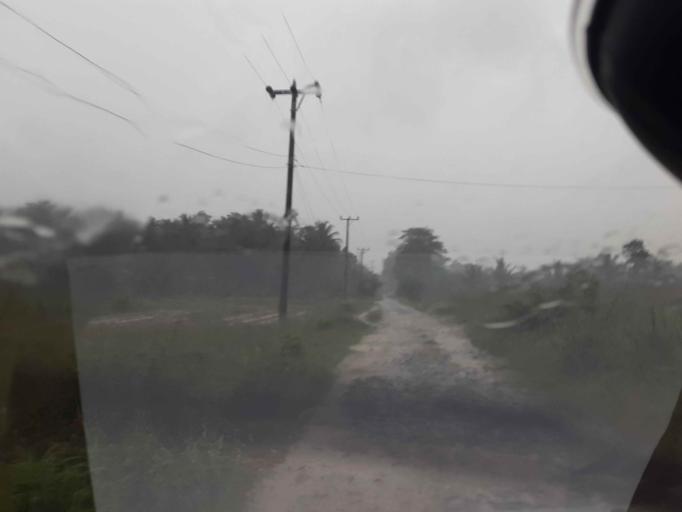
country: ID
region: Lampung
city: Kedaton
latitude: -5.3921
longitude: 105.3278
